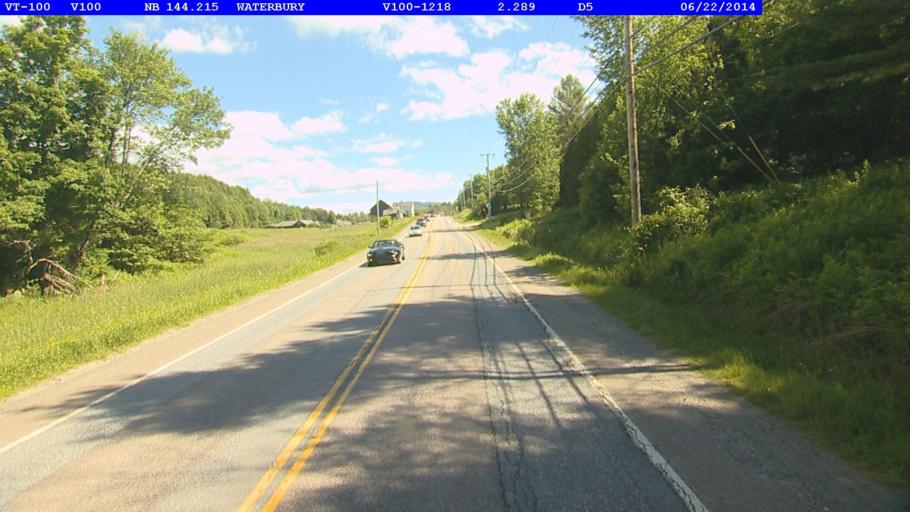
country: US
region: Vermont
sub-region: Washington County
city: Waterbury
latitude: 44.3643
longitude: -72.7313
